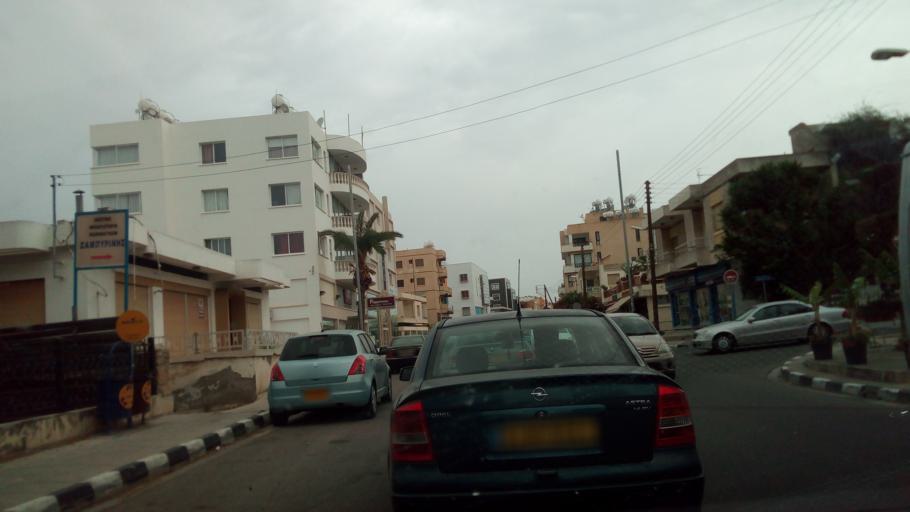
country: CY
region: Pafos
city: Paphos
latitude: 34.7726
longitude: 32.4307
